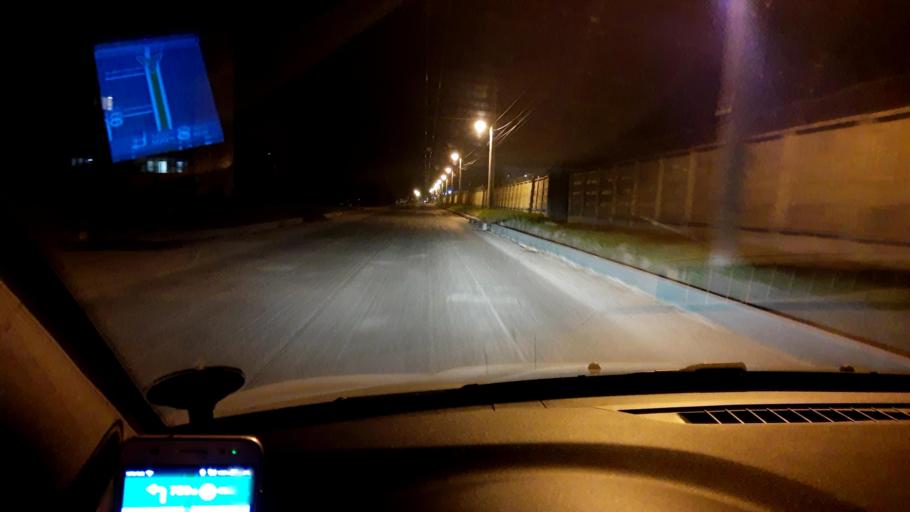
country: RU
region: Nizjnij Novgorod
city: Gorbatovka
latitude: 56.2955
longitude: 43.8671
